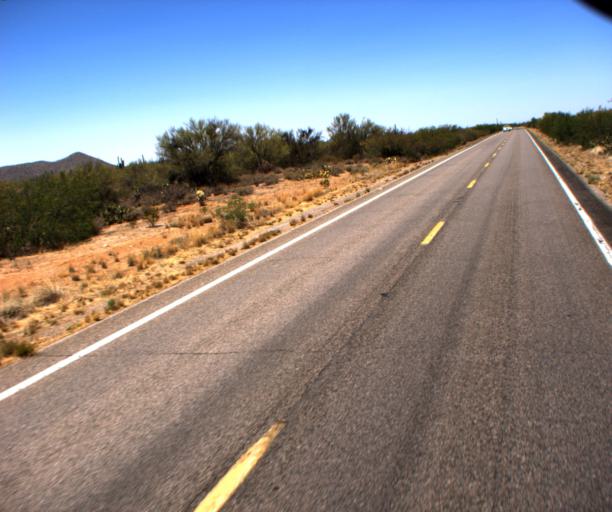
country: US
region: Arizona
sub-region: Pima County
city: Catalina
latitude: 32.7152
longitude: -111.1034
